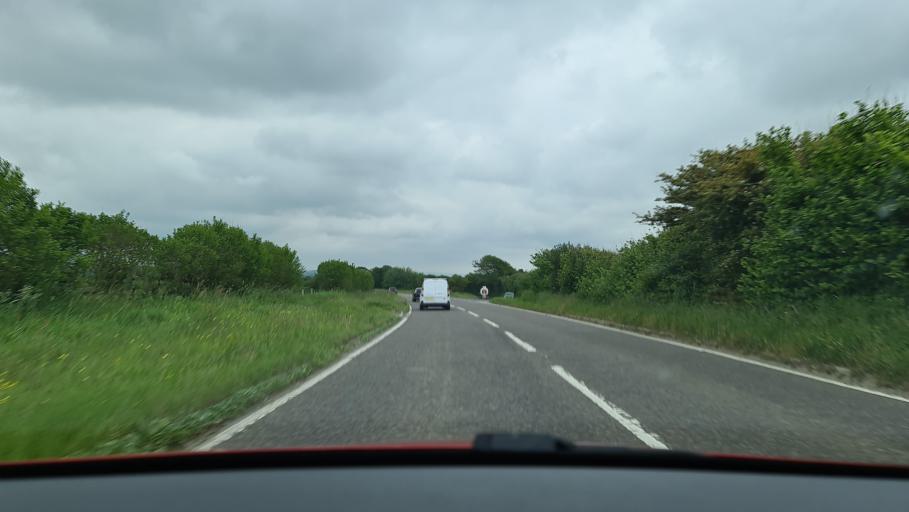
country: GB
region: England
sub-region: Cornwall
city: Camelford
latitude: 50.6349
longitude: -4.6620
